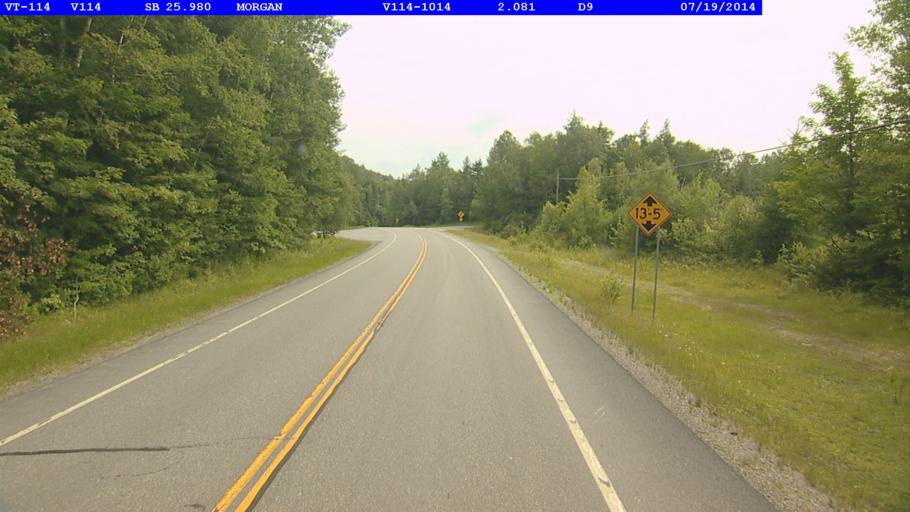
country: CA
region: Quebec
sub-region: Estrie
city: Coaticook
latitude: 44.8743
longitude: -71.9003
